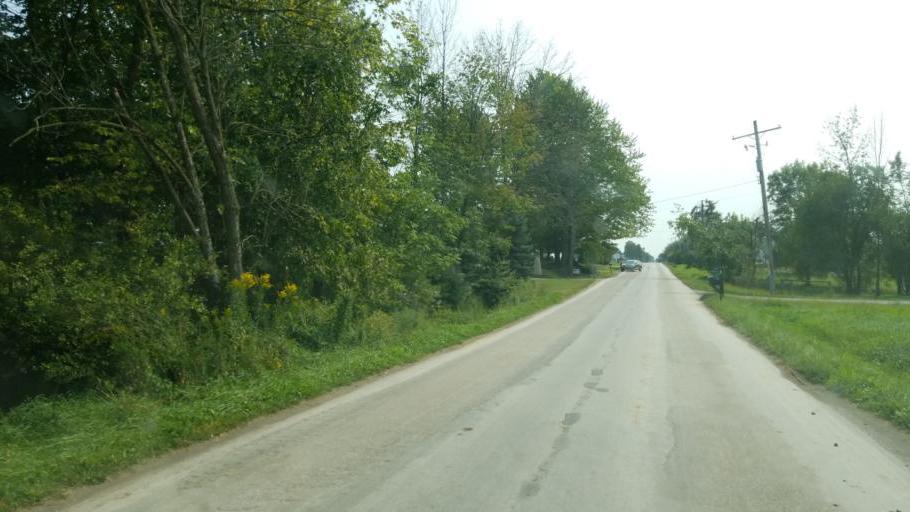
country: US
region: Ohio
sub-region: Geauga County
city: Middlefield
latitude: 41.4993
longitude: -81.0032
